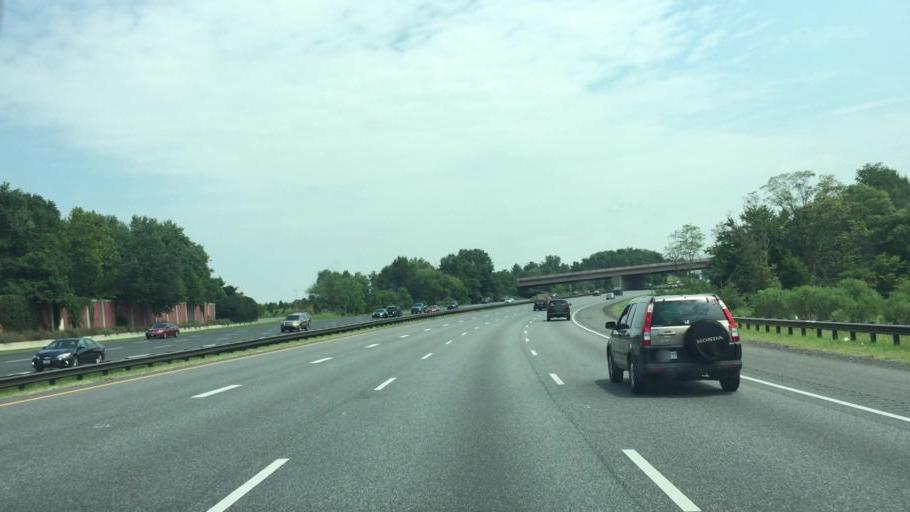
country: US
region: Maryland
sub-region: Prince George's County
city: Bowie
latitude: 38.9520
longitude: -76.7469
